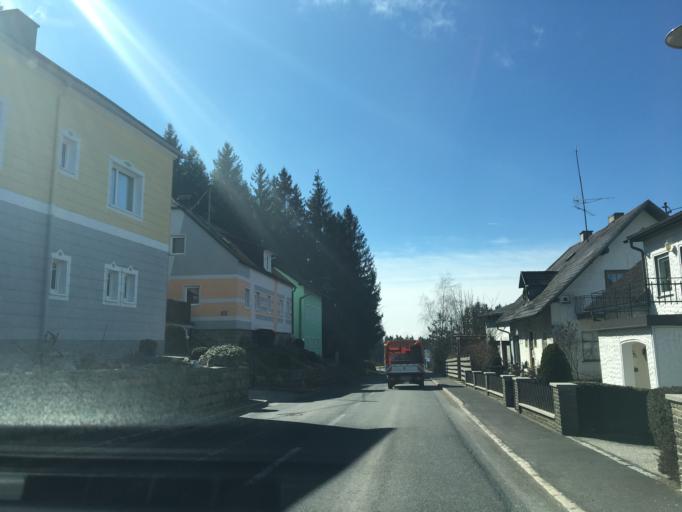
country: AT
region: Upper Austria
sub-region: Politischer Bezirk Perg
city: Sankt Georgen am Walde
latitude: 48.3046
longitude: 14.9062
